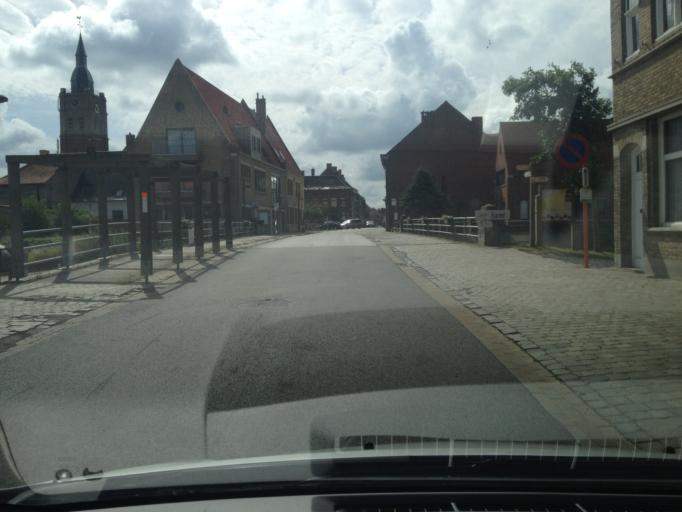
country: FR
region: Nord-Pas-de-Calais
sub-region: Departement du Nord
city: Hondschoote
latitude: 50.9203
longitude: 2.6226
